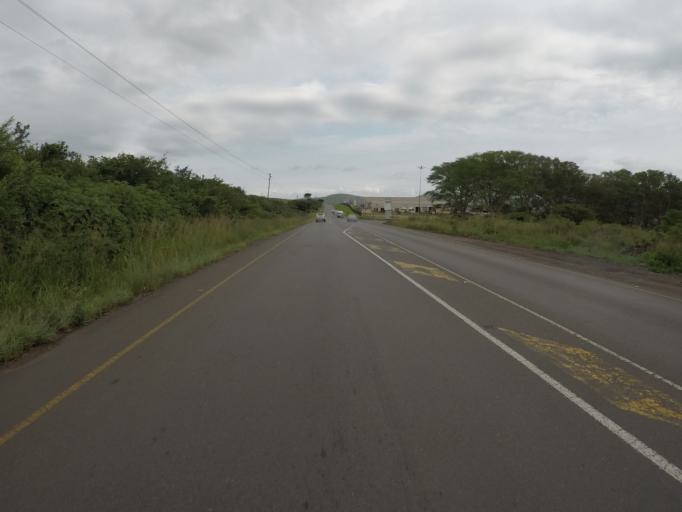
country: ZA
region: KwaZulu-Natal
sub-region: uThungulu District Municipality
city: Empangeni
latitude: -28.7295
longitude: 31.8712
